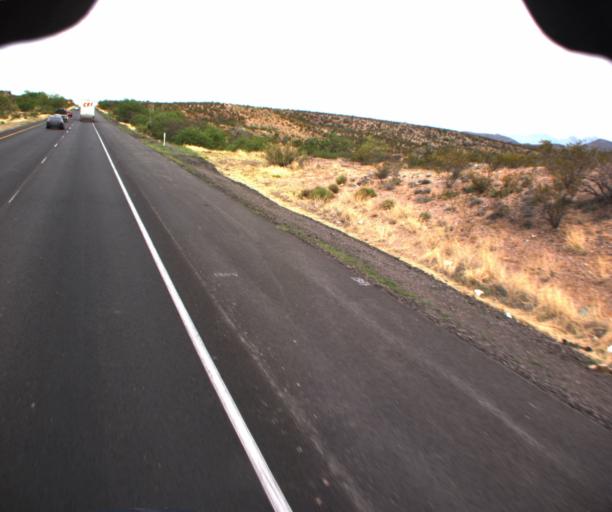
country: US
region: Arizona
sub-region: Pima County
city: Vail
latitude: 31.9951
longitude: -110.6136
